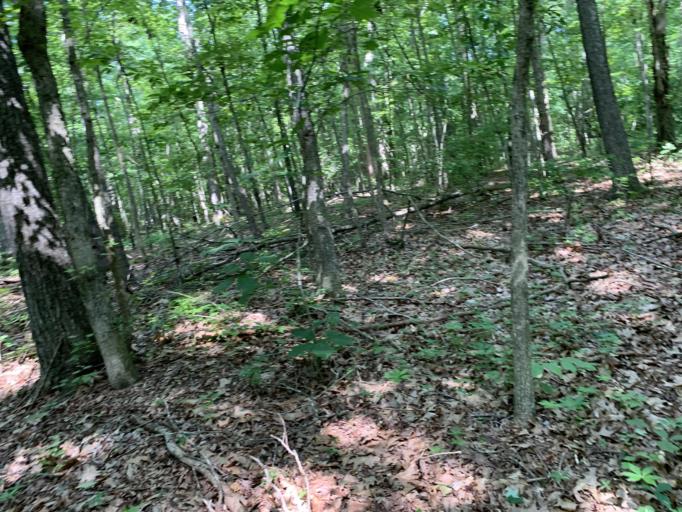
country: US
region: Delaware
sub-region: New Castle County
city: Townsend
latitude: 39.3374
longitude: -75.7182
